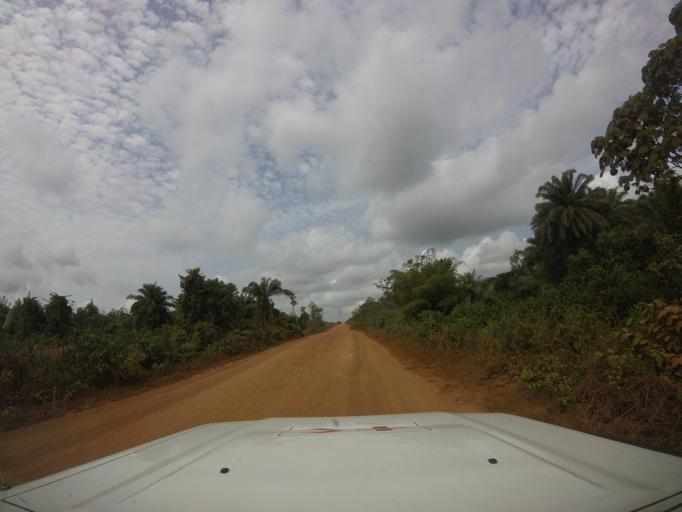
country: LR
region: Grand Cape Mount
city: Robertsport
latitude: 6.6993
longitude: -11.0964
